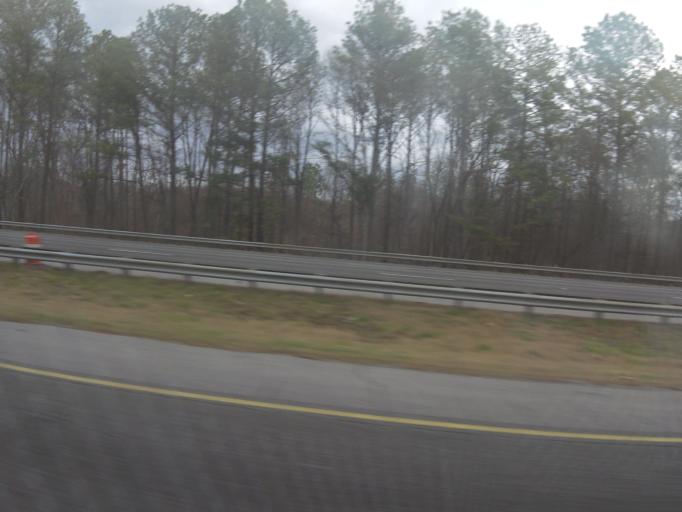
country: US
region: Georgia
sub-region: Whitfield County
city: Dalton
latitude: 34.6434
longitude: -84.9801
